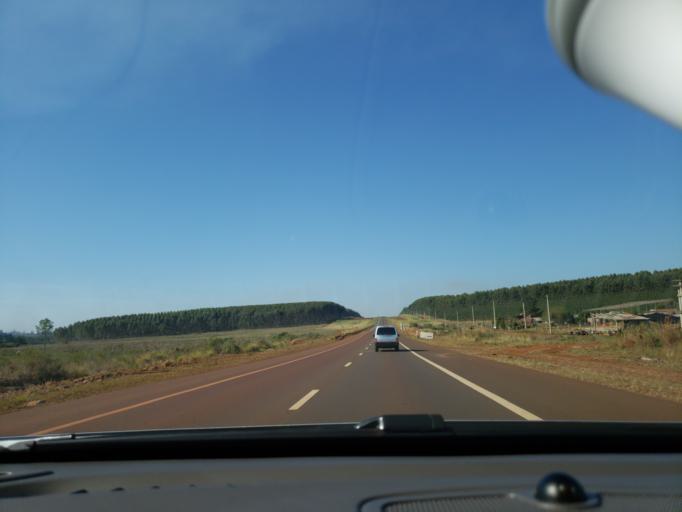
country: AR
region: Misiones
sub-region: Departamento de Capital
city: Posadas
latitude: -27.4652
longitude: -55.9642
